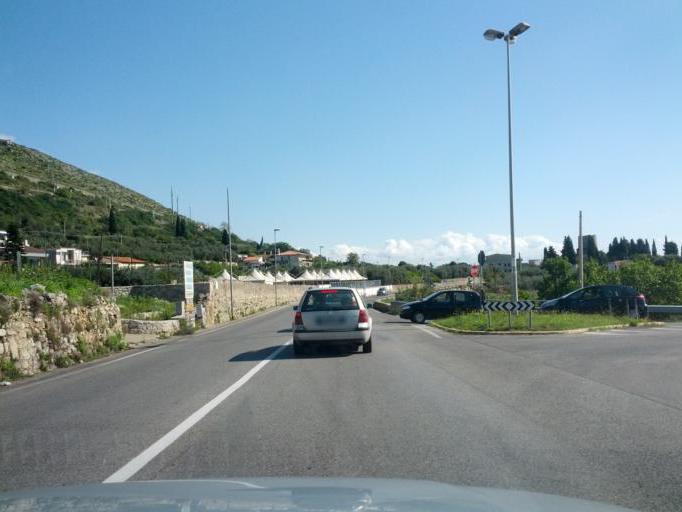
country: IT
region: Latium
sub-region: Provincia di Latina
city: Gaeta
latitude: 41.2528
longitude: 13.5745
